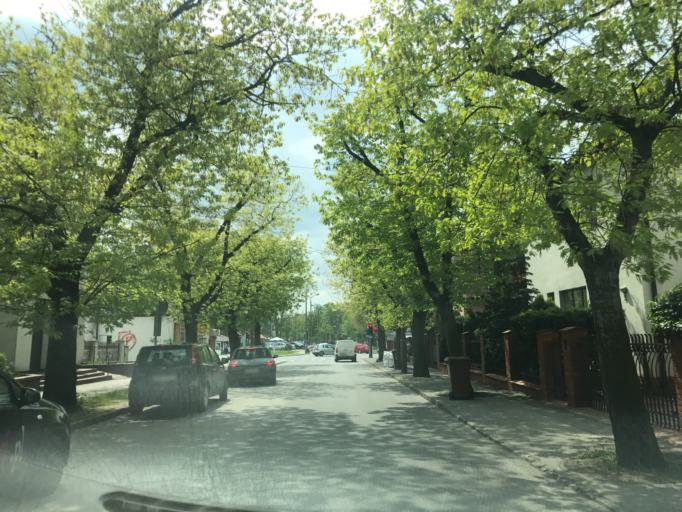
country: PL
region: Kujawsko-Pomorskie
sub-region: Bydgoszcz
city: Bydgoszcz
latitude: 53.1301
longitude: 18.0292
